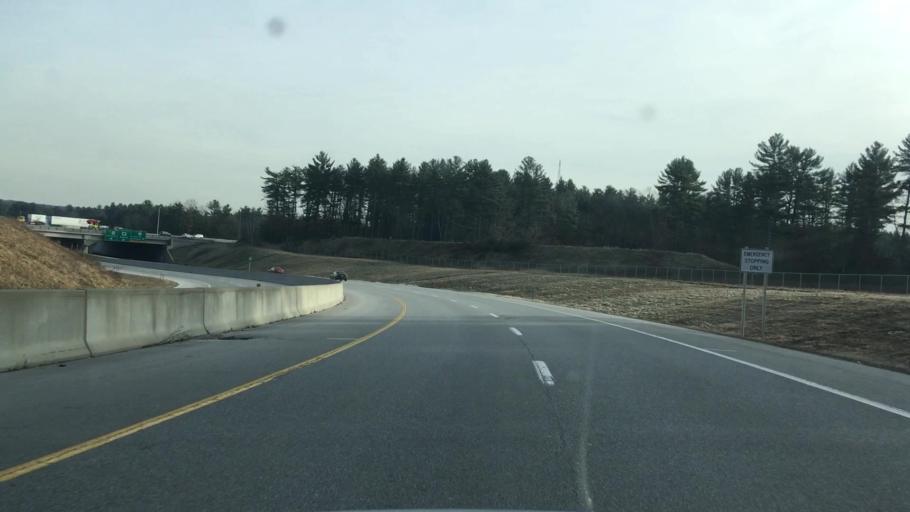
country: US
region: New Hampshire
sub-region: Hillsborough County
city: East Merrimack
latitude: 42.9147
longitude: -71.4683
